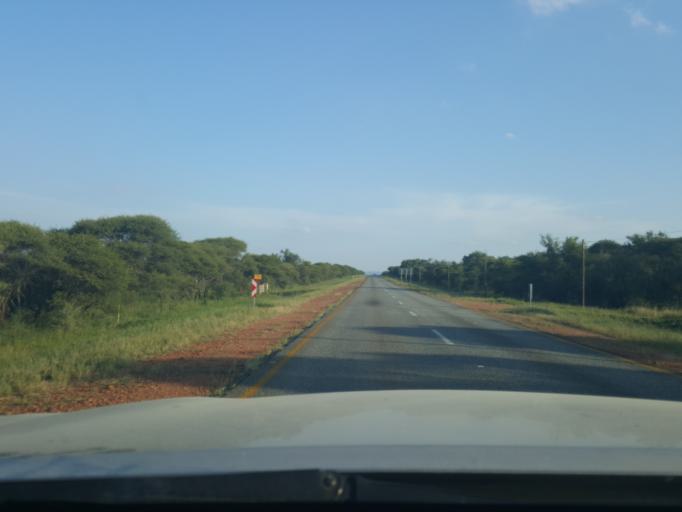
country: BW
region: South East
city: Ramotswa
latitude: -25.1247
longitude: 26.1532
